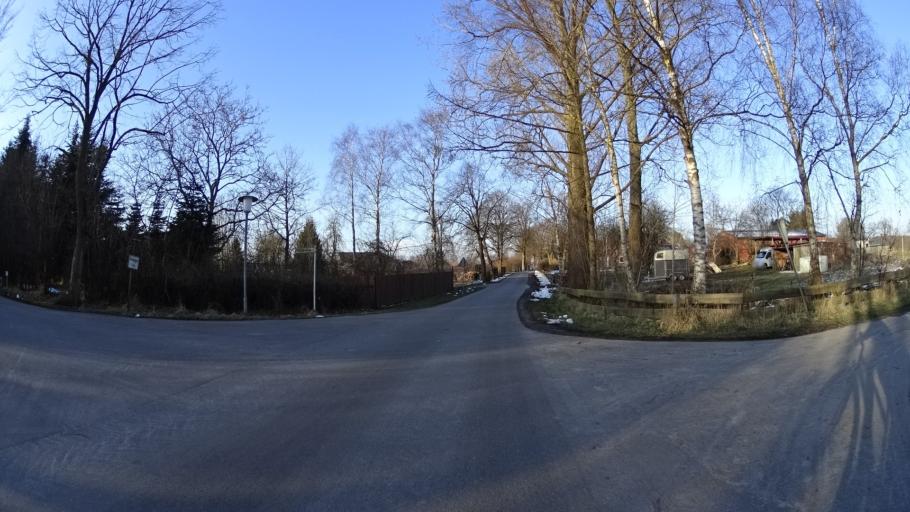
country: DE
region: Schleswig-Holstein
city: Fargau-Pratjau
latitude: 54.3425
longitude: 10.4084
